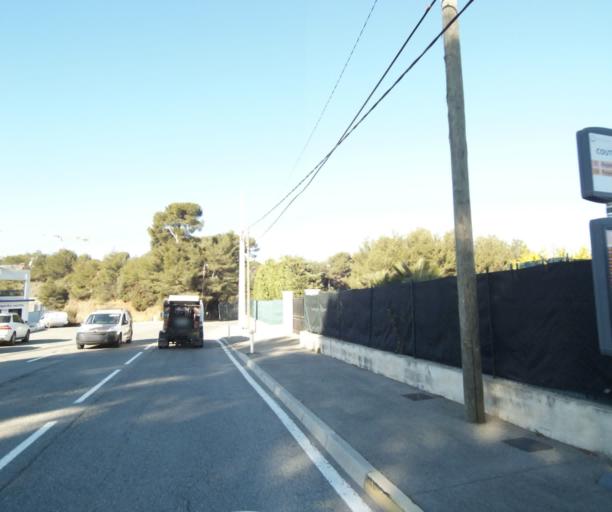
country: FR
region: Provence-Alpes-Cote d'Azur
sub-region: Departement des Alpes-Maritimes
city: Biot
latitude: 43.6048
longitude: 7.0912
